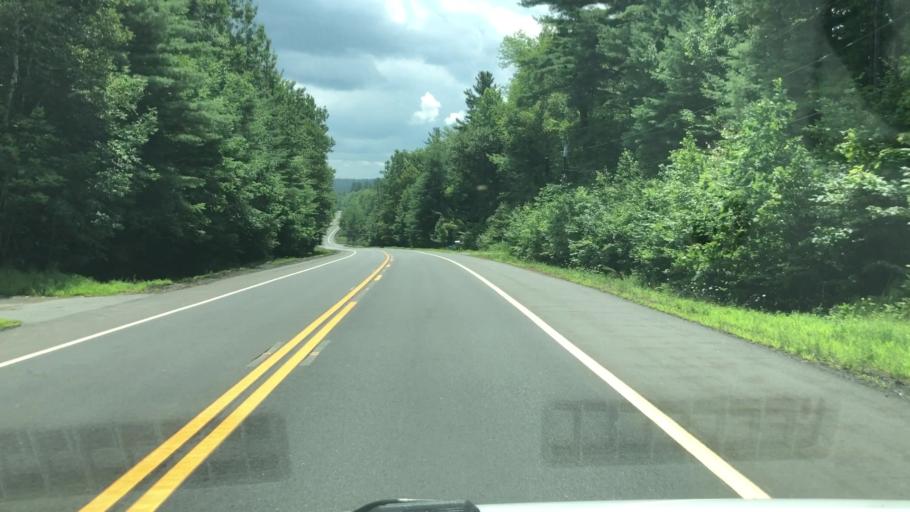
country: US
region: Massachusetts
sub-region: Franklin County
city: Ashfield
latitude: 42.4827
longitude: -72.8102
